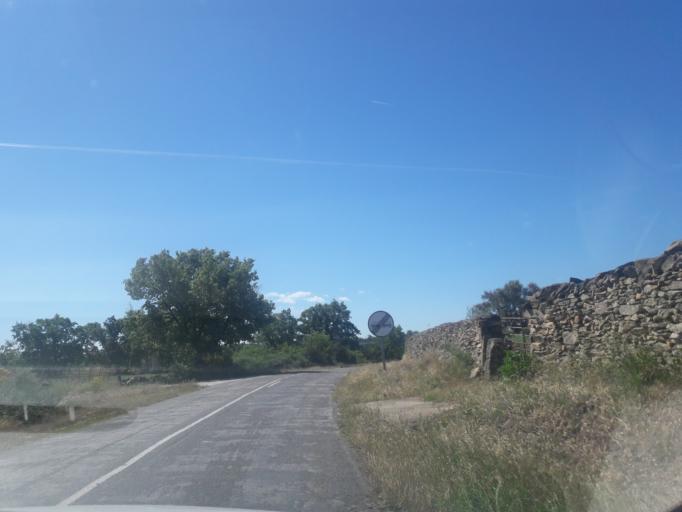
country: ES
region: Castille and Leon
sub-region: Provincia de Salamanca
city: Lumbrales
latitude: 40.9488
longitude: -6.7170
